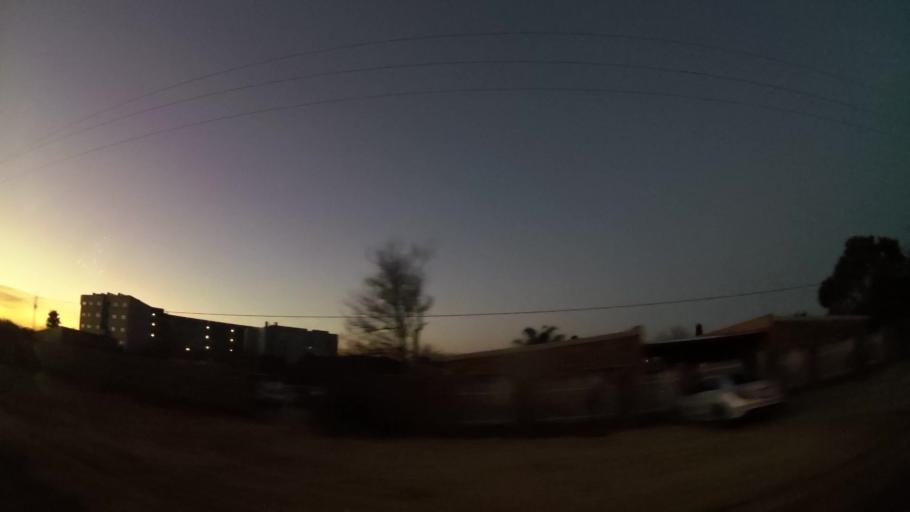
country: ZA
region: Gauteng
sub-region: City of Johannesburg Metropolitan Municipality
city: Roodepoort
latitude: -26.1858
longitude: 27.9223
